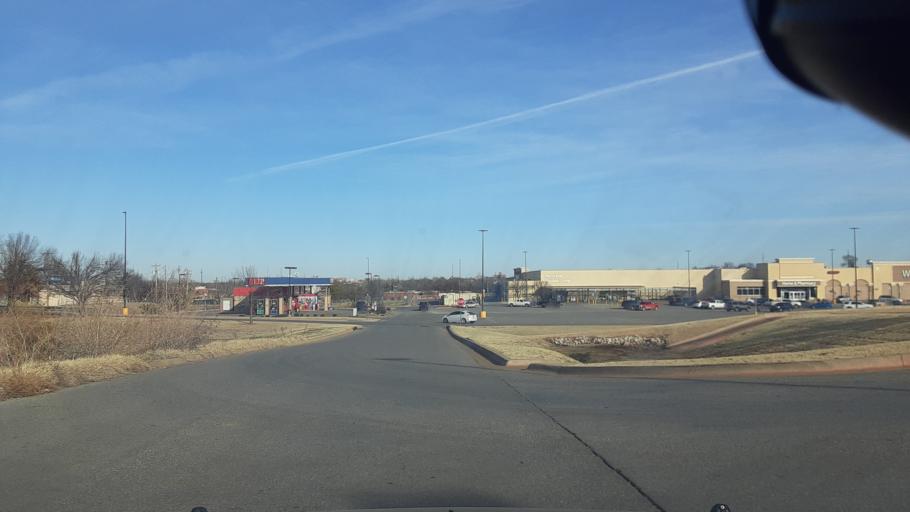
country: US
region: Oklahoma
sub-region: Logan County
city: Guthrie
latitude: 35.8607
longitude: -97.4241
